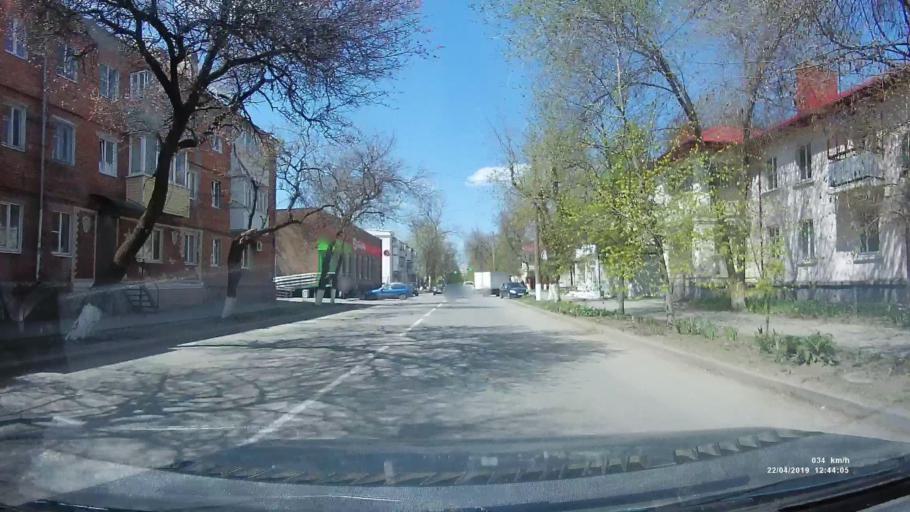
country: RU
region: Rostov
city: Azov
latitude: 47.1030
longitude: 39.4195
